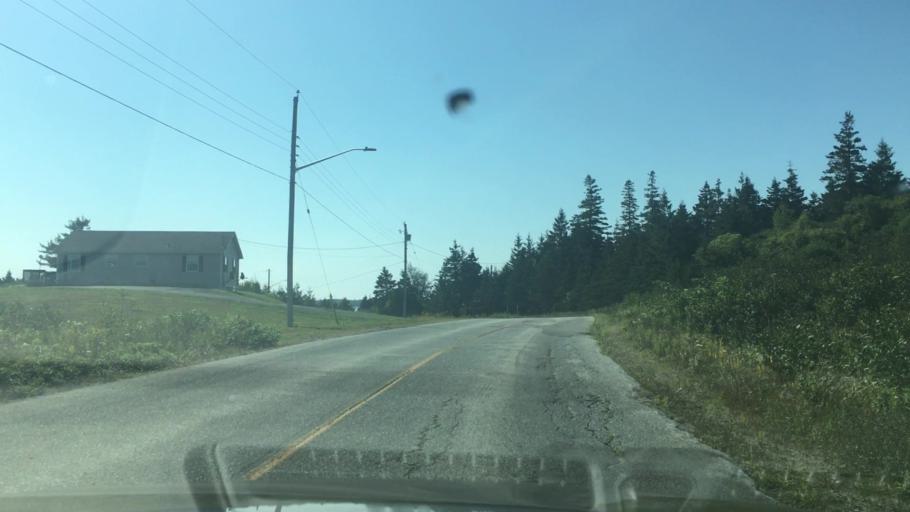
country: CA
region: Nova Scotia
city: New Glasgow
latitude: 44.8026
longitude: -62.6931
